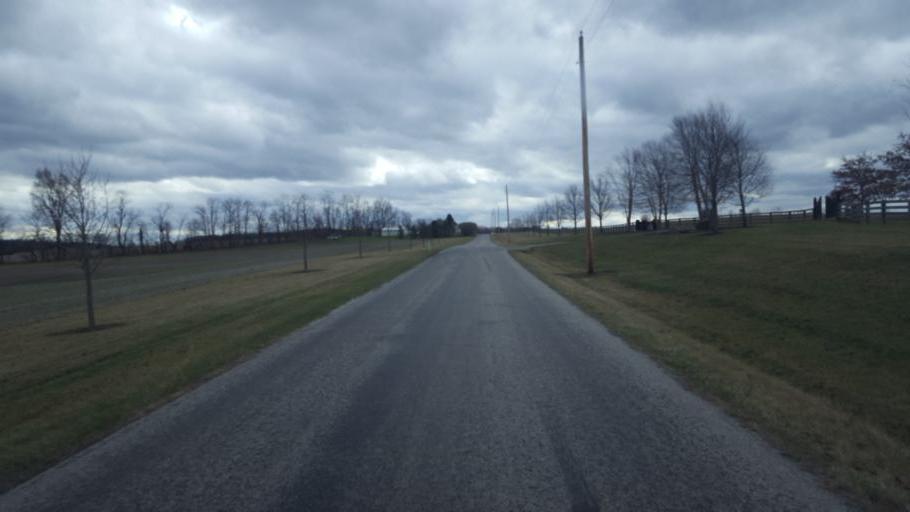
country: US
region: Ohio
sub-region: Licking County
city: Utica
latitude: 40.2325
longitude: -82.4082
